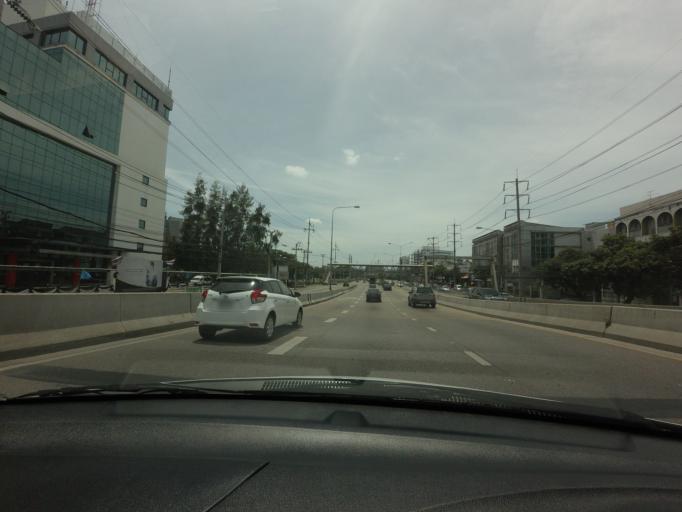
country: TH
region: Bangkok
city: Lak Si
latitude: 13.8857
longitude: 100.5788
